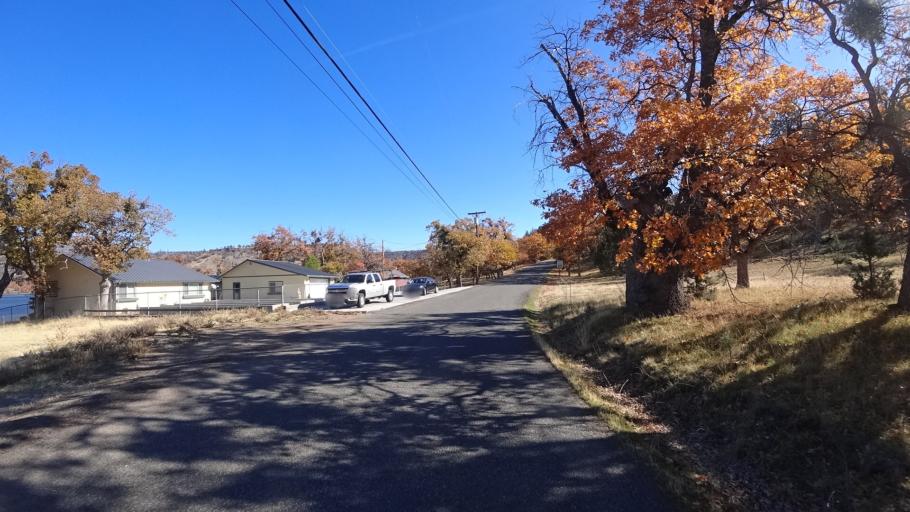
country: US
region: California
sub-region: Siskiyou County
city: Montague
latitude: 41.9796
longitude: -122.3153
